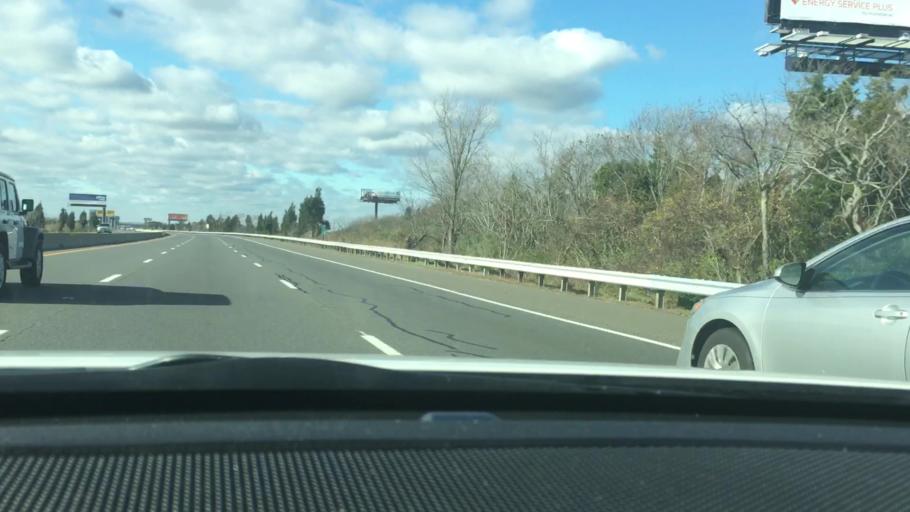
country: US
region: New Jersey
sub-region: Atlantic County
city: Ventnor City
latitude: 39.3690
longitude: -74.4636
